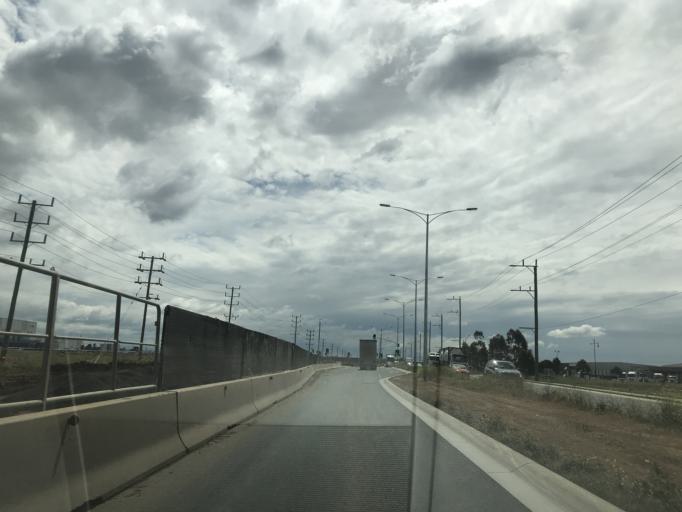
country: AU
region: Victoria
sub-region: Wyndham
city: Truganina
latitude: -37.8045
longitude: 144.7516
